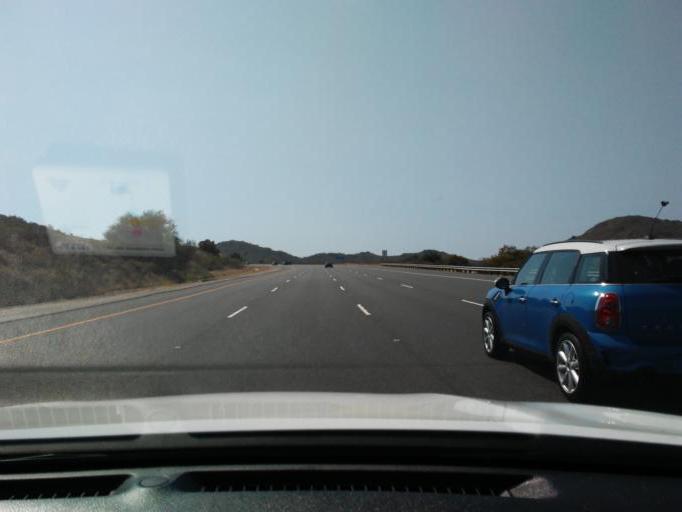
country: US
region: California
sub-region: Orange County
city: Laguna Woods
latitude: 33.5967
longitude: -117.7658
